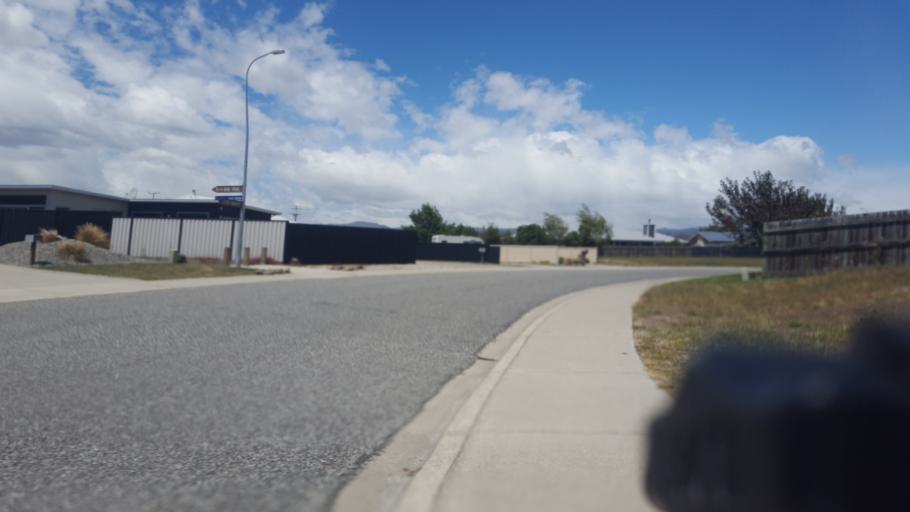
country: NZ
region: Otago
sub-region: Queenstown-Lakes District
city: Wanaka
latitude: -45.1943
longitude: 169.3334
